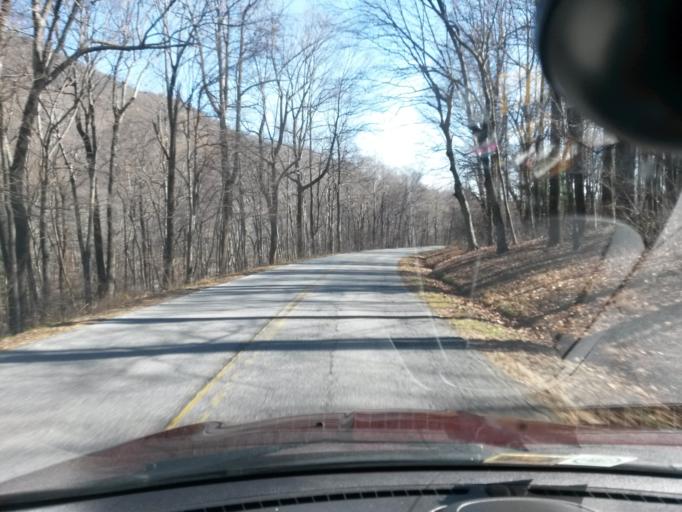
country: US
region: Virginia
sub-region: Botetourt County
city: Buchanan
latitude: 37.4438
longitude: -79.6022
